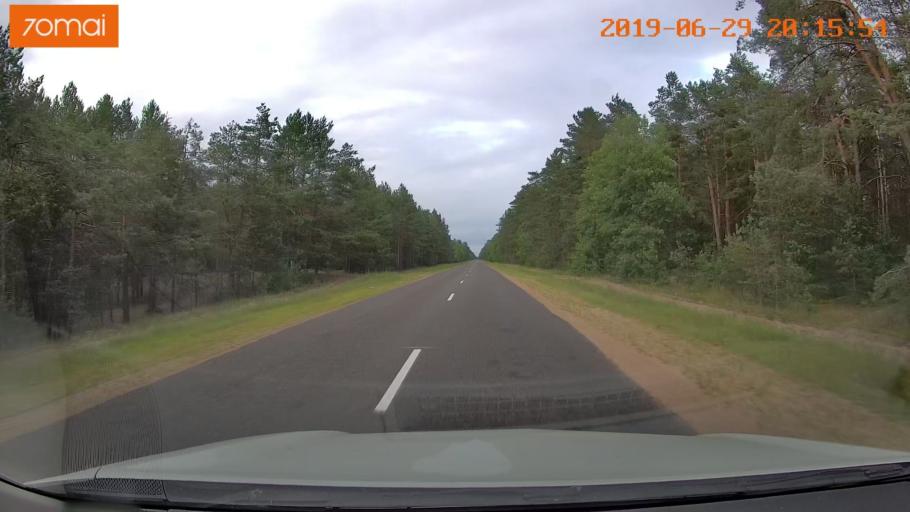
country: BY
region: Brest
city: Asnyezhytsy
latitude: 52.3775
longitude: 26.1854
